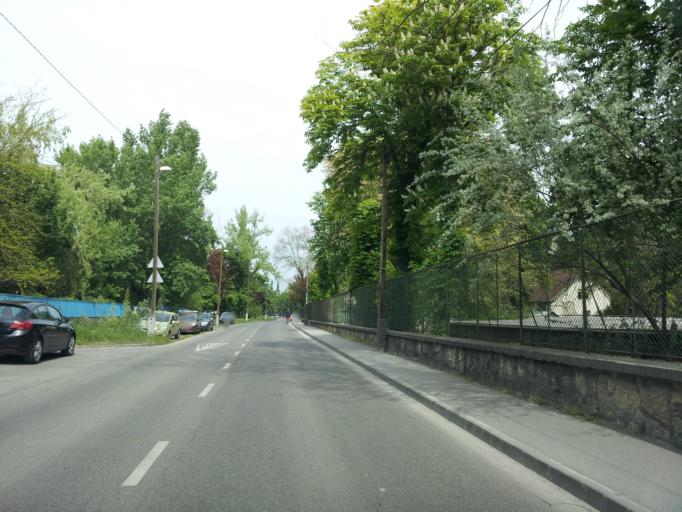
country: HU
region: Pest
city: Budakalasz
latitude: 47.5948
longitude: 19.0670
